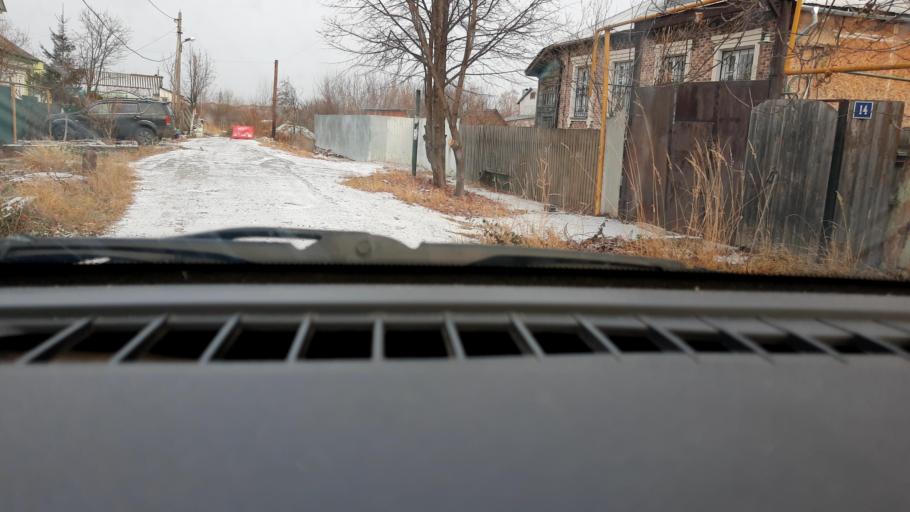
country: RU
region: Nizjnij Novgorod
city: Gorbatovka
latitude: 56.2763
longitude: 43.8777
